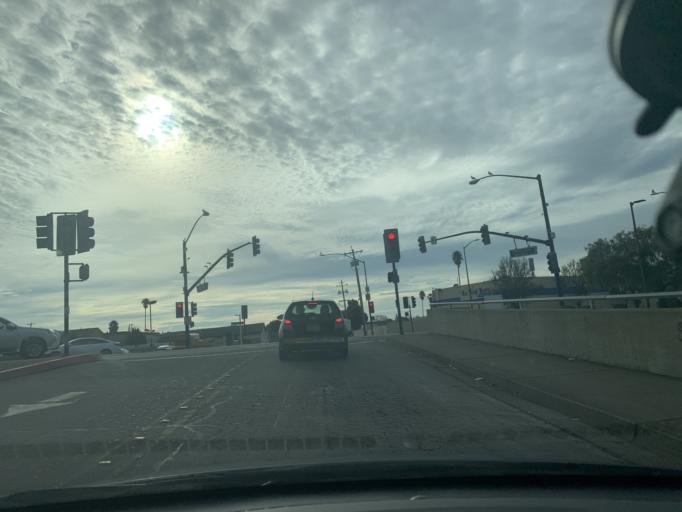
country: US
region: California
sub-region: Contra Costa County
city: Rollingwood
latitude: 37.9553
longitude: -122.3312
